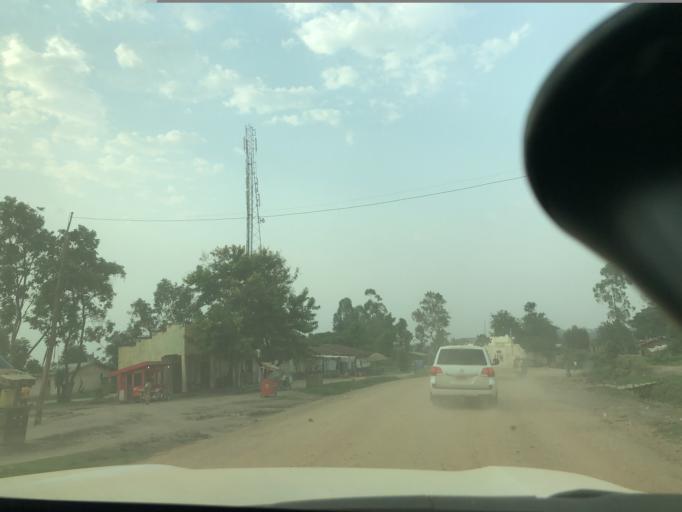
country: UG
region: Western Region
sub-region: Kasese District
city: Margherita
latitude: 0.3312
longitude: 29.6747
